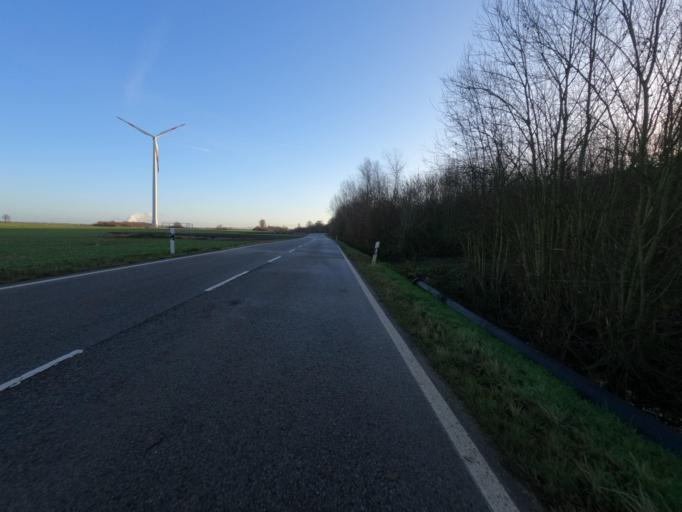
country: DE
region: North Rhine-Westphalia
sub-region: Regierungsbezirk Koln
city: Niederzier
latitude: 50.9359
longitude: 6.4934
